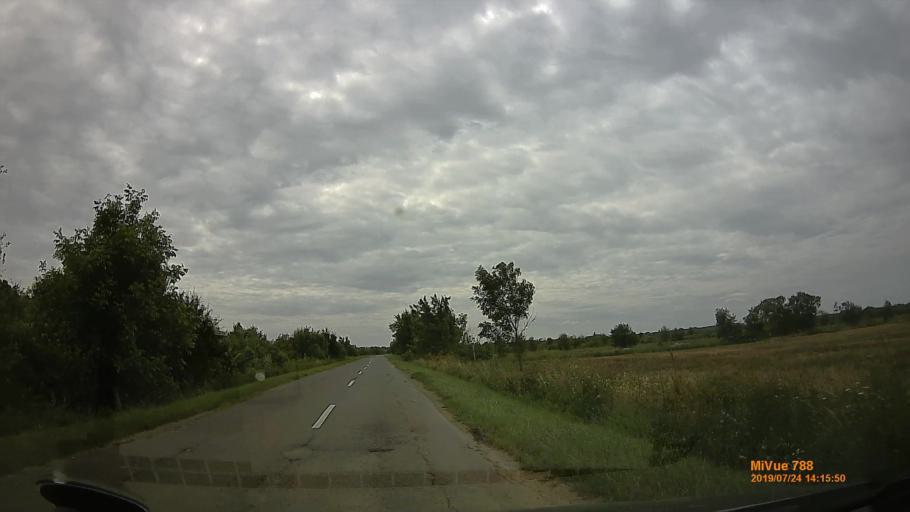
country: UA
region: Zakarpattia
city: Batiovo
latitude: 48.3201
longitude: 22.3019
